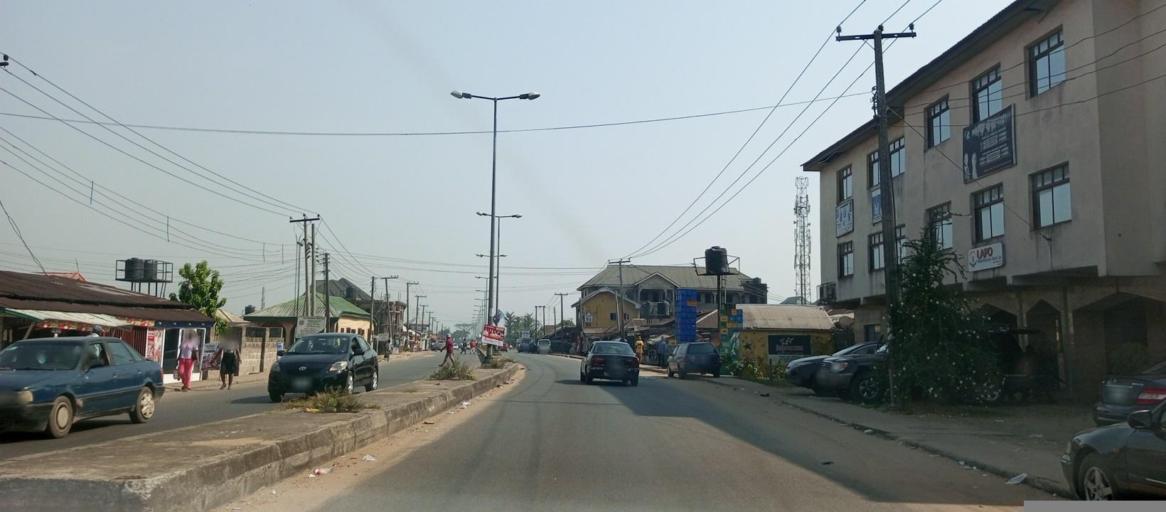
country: NG
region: Rivers
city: Emuoha
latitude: 4.8901
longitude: 6.9029
